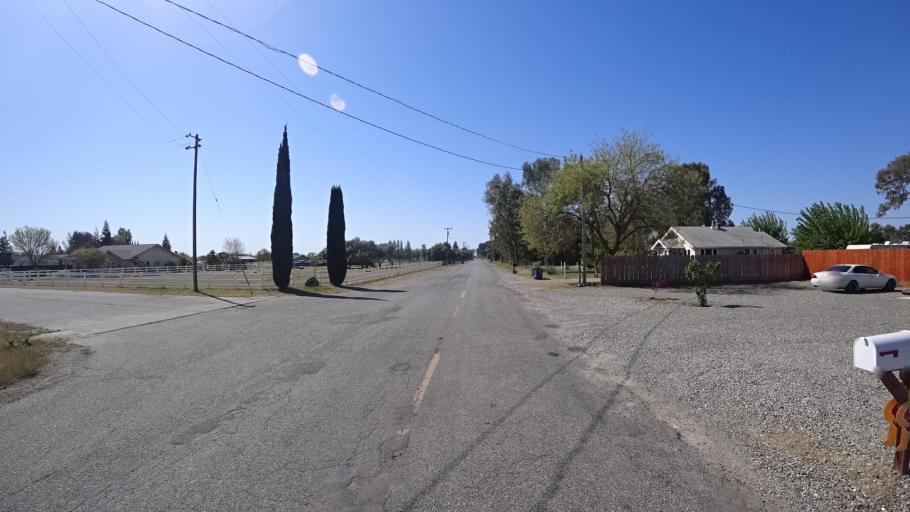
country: US
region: California
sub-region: Glenn County
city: Orland
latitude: 39.7295
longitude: -122.1923
